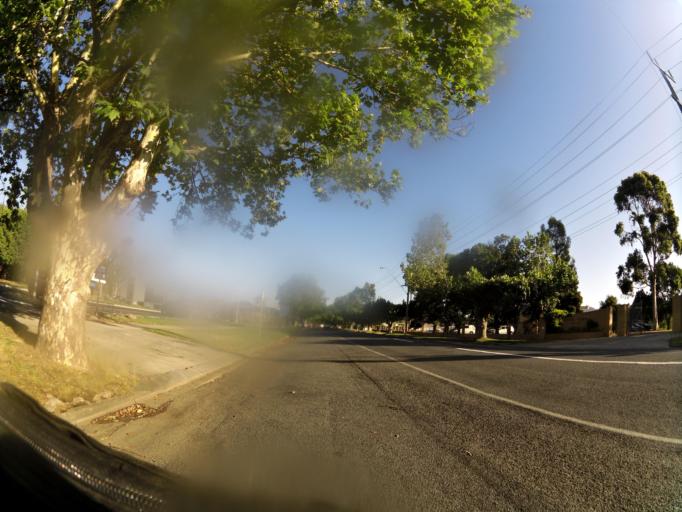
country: AU
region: Victoria
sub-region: Murrindindi
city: Kinglake West
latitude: -37.0217
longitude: 145.1311
